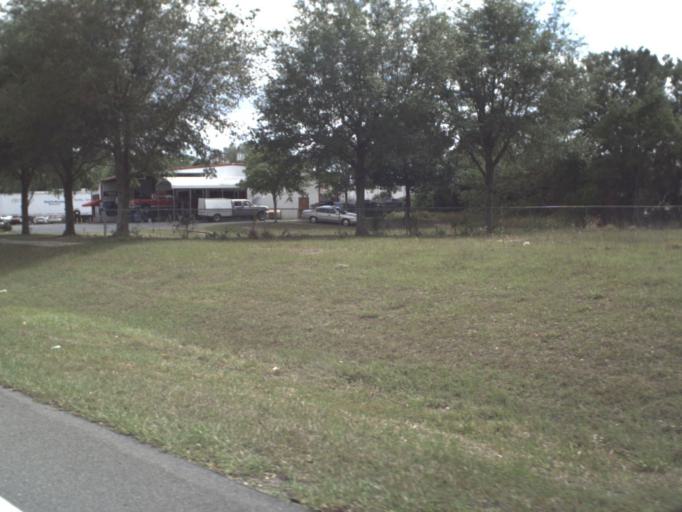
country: US
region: Florida
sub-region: Marion County
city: Ocala
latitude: 29.2083
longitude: -82.1425
